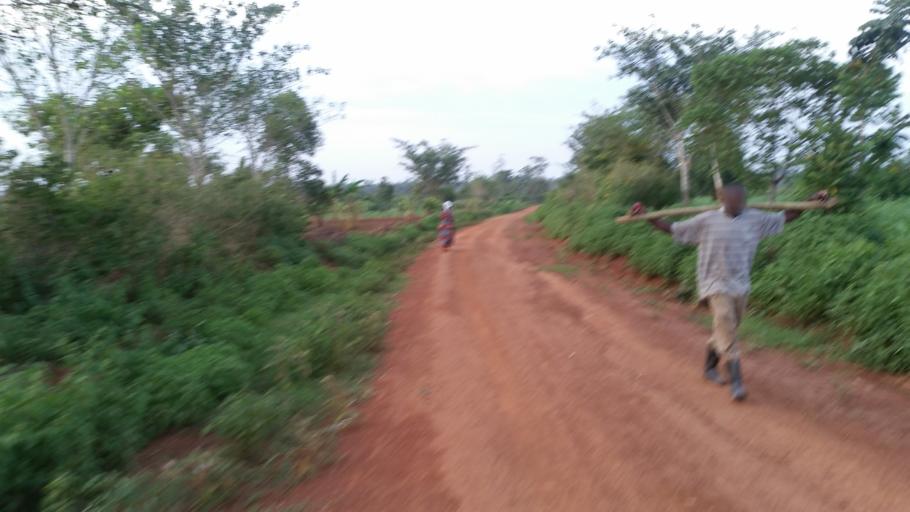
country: UG
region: Eastern Region
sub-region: Busia District
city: Busia
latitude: 0.5394
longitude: 34.0427
